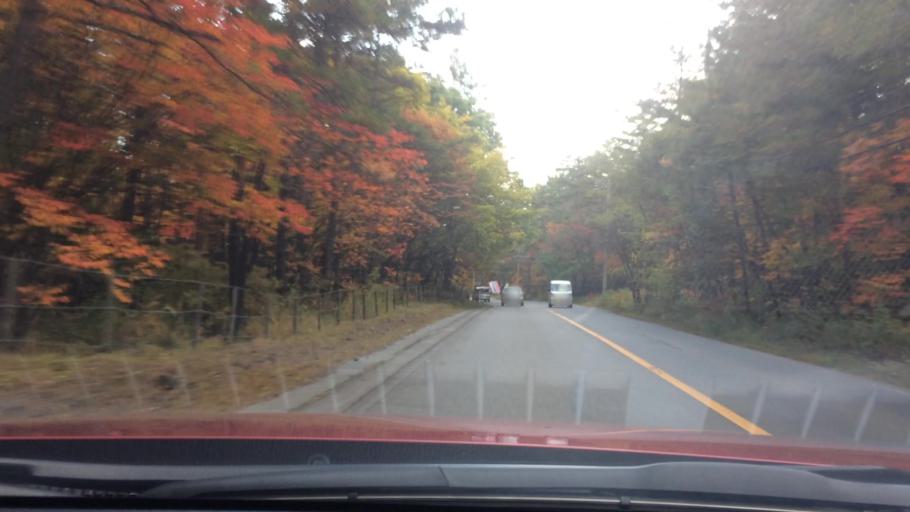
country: JP
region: Nagano
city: Komoro
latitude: 36.4363
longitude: 138.5746
